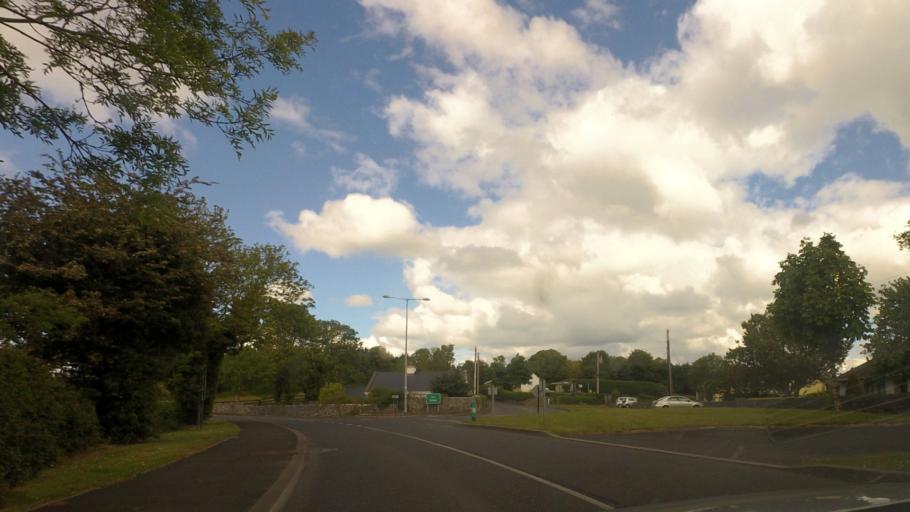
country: IE
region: Munster
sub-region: An Clar
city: Ennis
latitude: 52.8356
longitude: -9.0066
